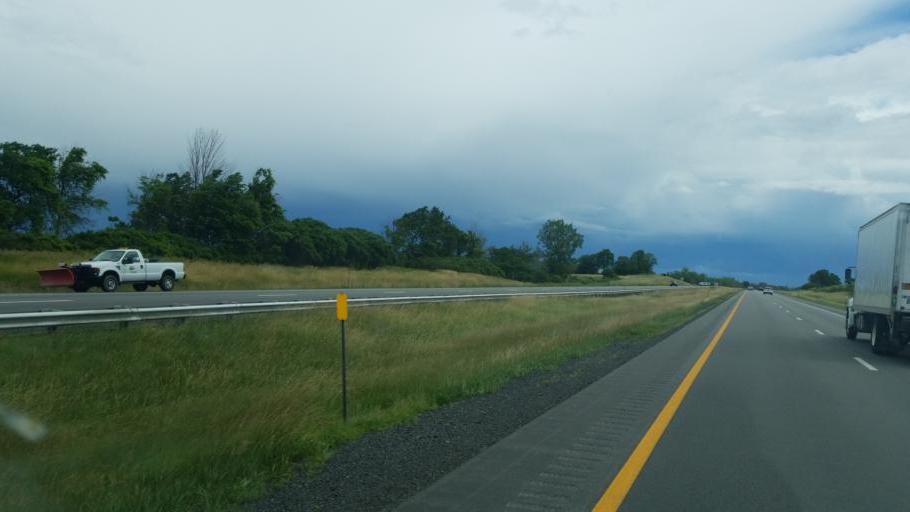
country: US
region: New York
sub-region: Monroe County
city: Scottsville
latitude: 43.0376
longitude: -77.8078
